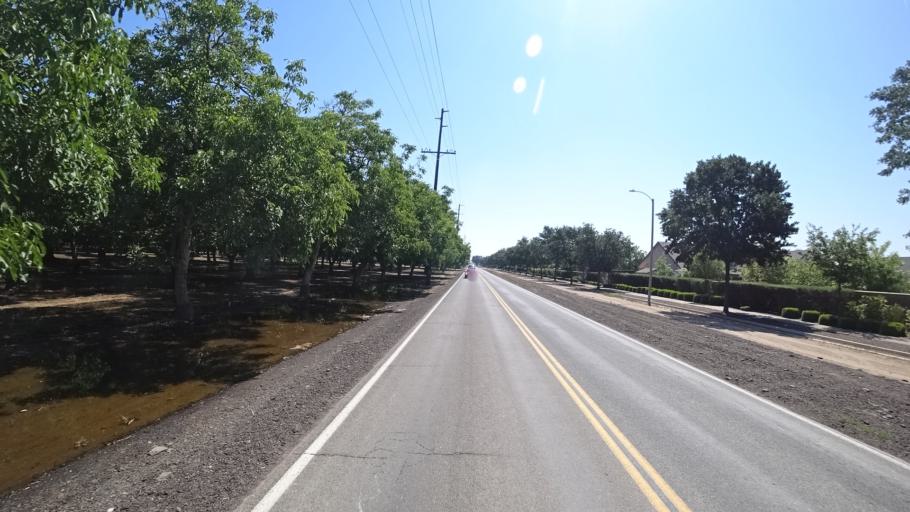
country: US
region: California
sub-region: Kings County
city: Lucerne
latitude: 36.3719
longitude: -119.6520
